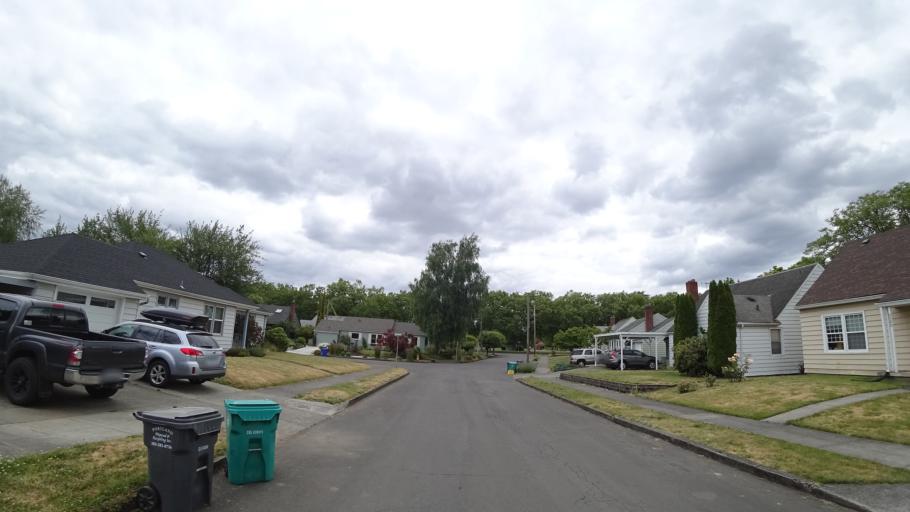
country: US
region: Oregon
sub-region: Multnomah County
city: Portland
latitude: 45.5761
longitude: -122.7147
